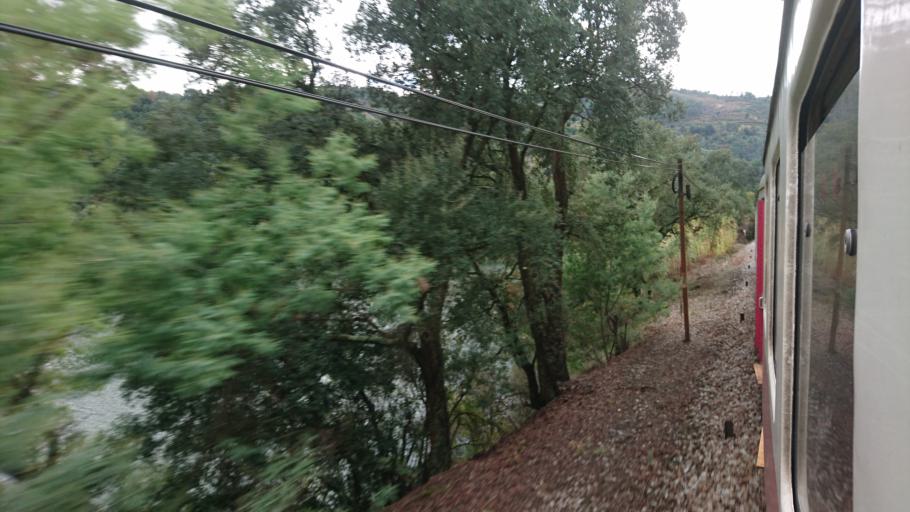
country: PT
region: Viseu
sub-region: Cinfaes
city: Cinfaes
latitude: 41.0928
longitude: -8.0464
